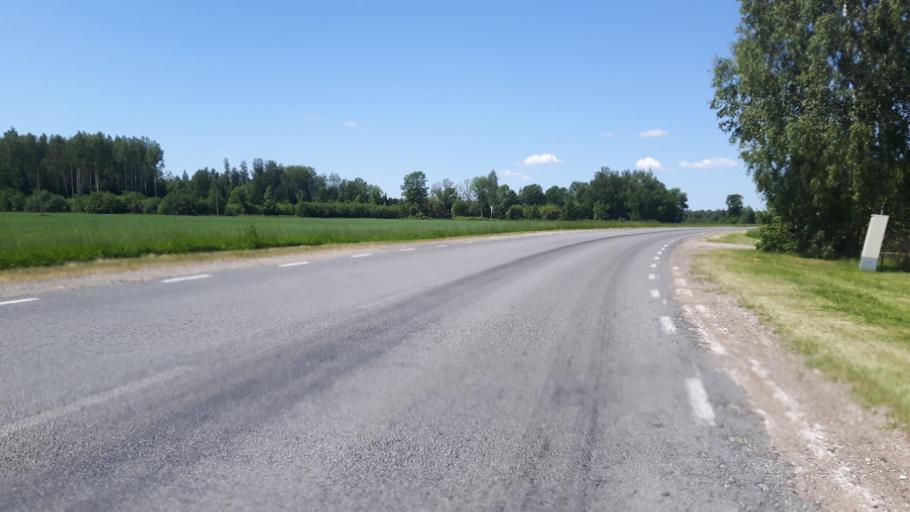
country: EE
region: Paernumaa
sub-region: Tootsi vald
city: Tootsi
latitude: 58.4944
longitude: 24.8885
